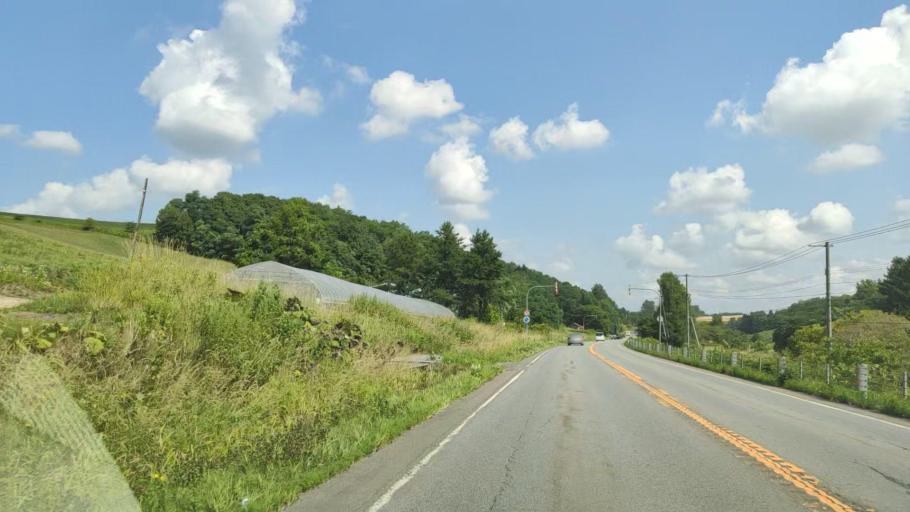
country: JP
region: Hokkaido
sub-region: Asahikawa-shi
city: Asahikawa
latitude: 43.5664
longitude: 142.4350
